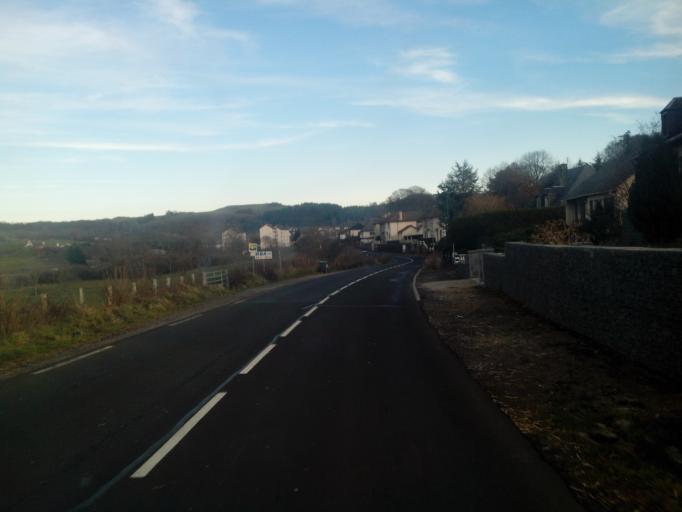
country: FR
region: Auvergne
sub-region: Departement du Cantal
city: Riom-es-Montagnes
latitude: 45.2855
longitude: 2.6421
